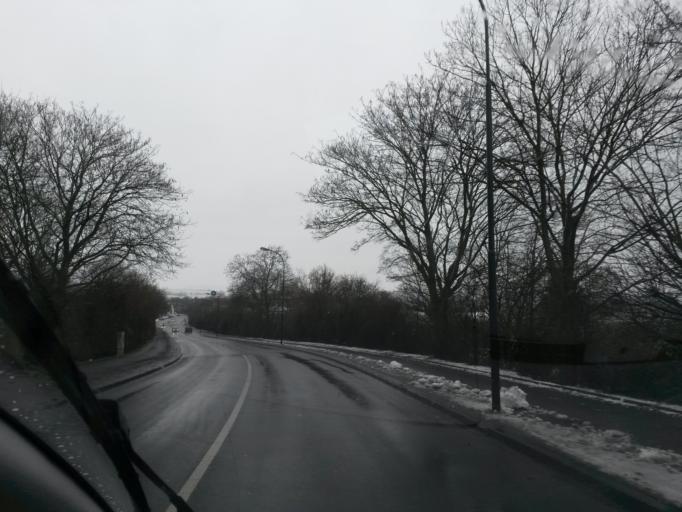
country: DE
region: Hesse
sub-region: Regierungsbezirk Kassel
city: Fulda
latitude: 50.5377
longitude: 9.6878
